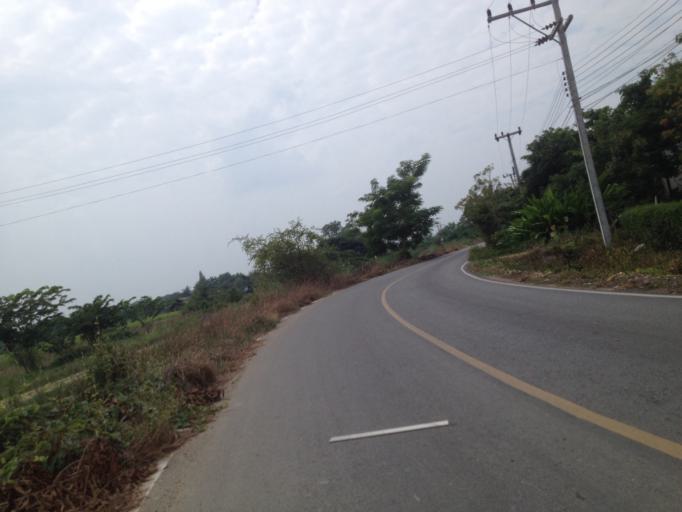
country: TH
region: Chiang Mai
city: San Pa Tong
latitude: 18.6569
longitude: 98.8750
